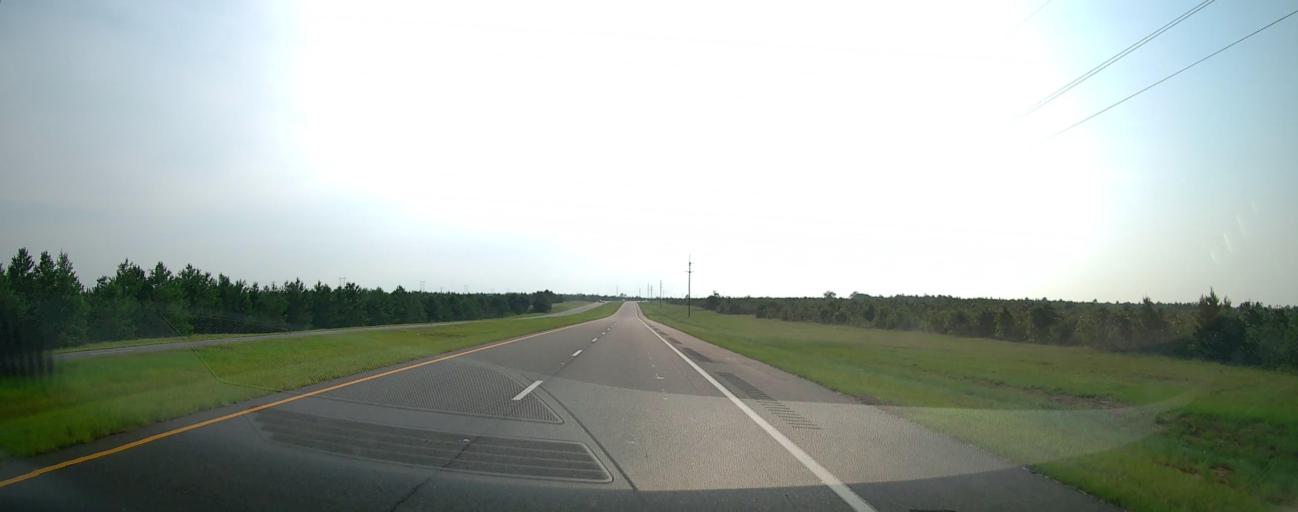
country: US
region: Georgia
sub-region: Talbot County
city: Talbotton
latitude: 32.5948
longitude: -84.4291
